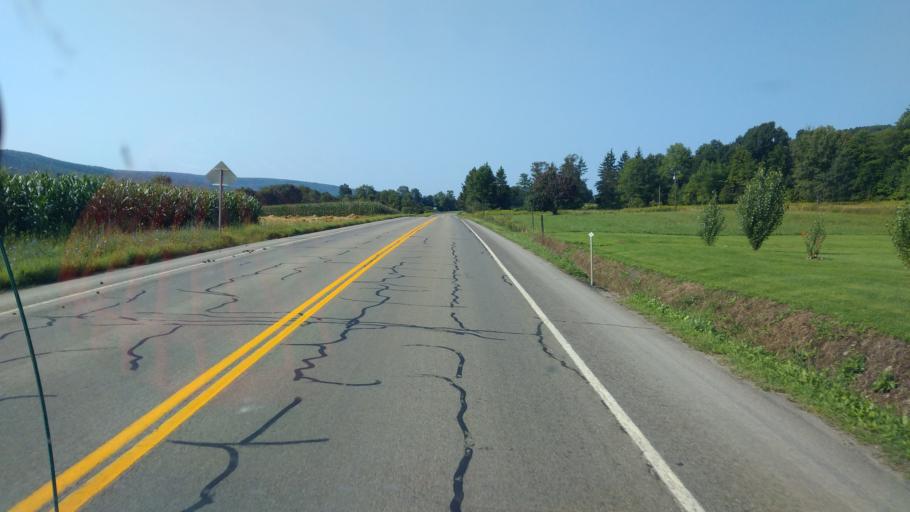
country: US
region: New York
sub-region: Allegany County
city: Friendship
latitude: 42.2989
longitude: -78.1899
